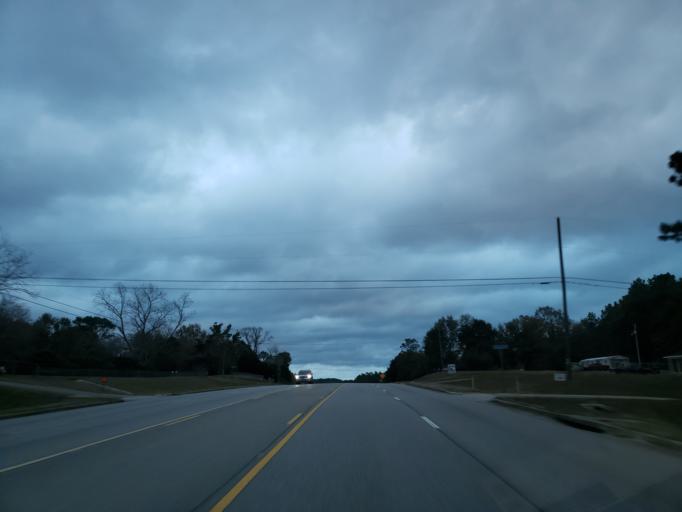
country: US
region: Alabama
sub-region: Mobile County
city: Chickasaw
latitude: 30.8001
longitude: -88.2254
